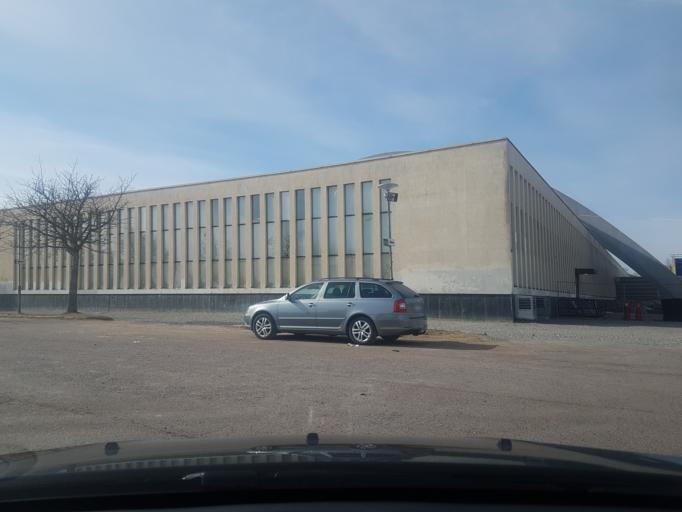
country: SE
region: Dalarna
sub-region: Borlange Kommun
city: Borlaenge
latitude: 60.4927
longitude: 15.4128
